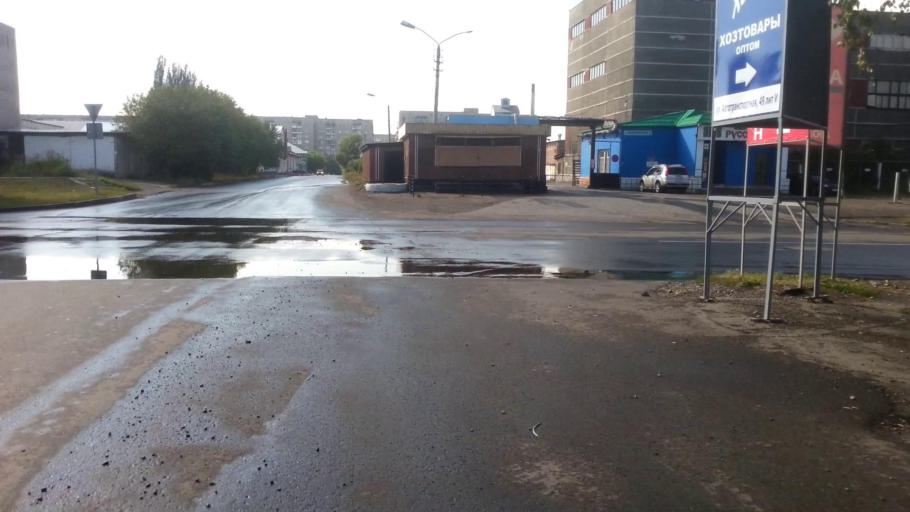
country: RU
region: Altai Krai
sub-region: Gorod Barnaulskiy
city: Barnaul
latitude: 53.3449
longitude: 83.7153
